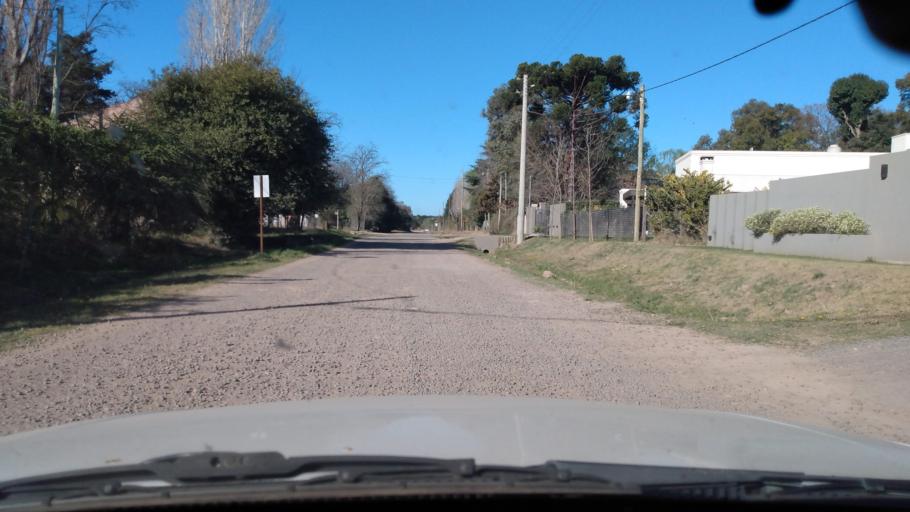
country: AR
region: Buenos Aires
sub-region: Partido de Mercedes
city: Mercedes
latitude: -34.6485
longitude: -59.4005
